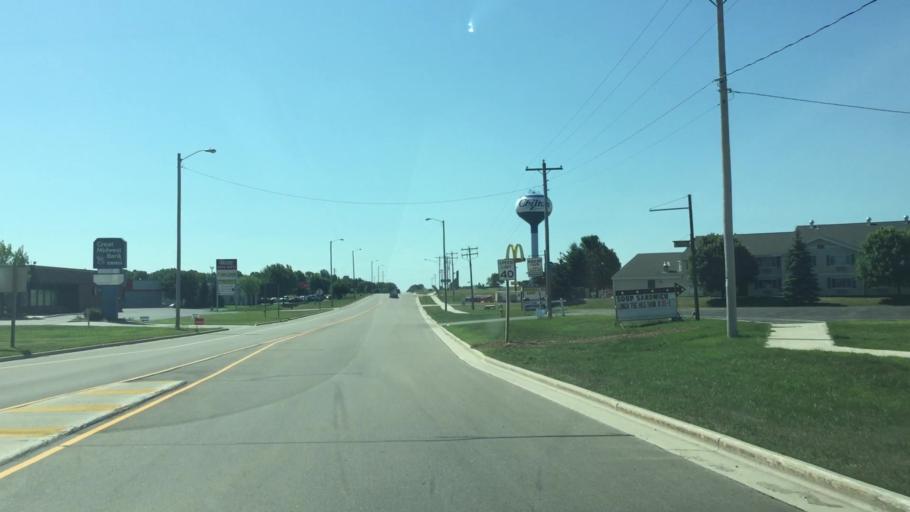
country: US
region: Wisconsin
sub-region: Calumet County
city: Chilton
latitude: 44.0218
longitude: -88.1545
